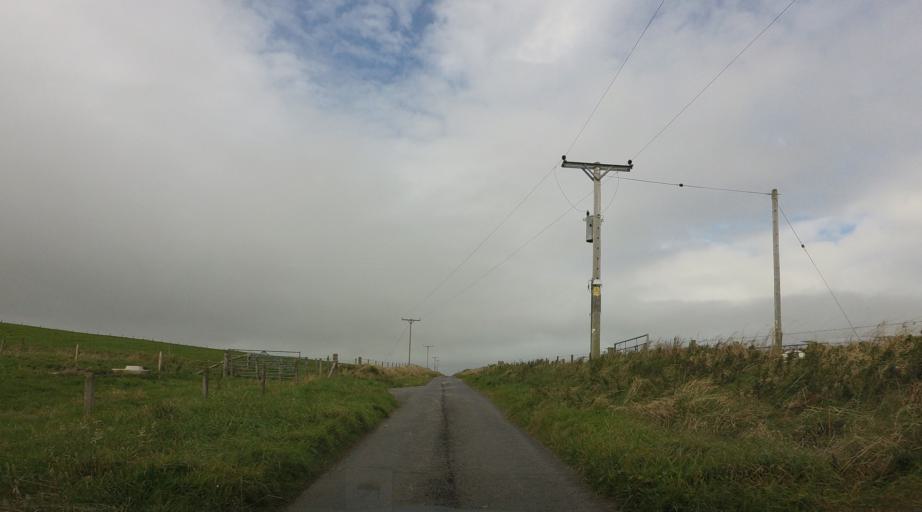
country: GB
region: Scotland
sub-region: Orkney Islands
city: Kirkwall
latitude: 58.8075
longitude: -2.9264
